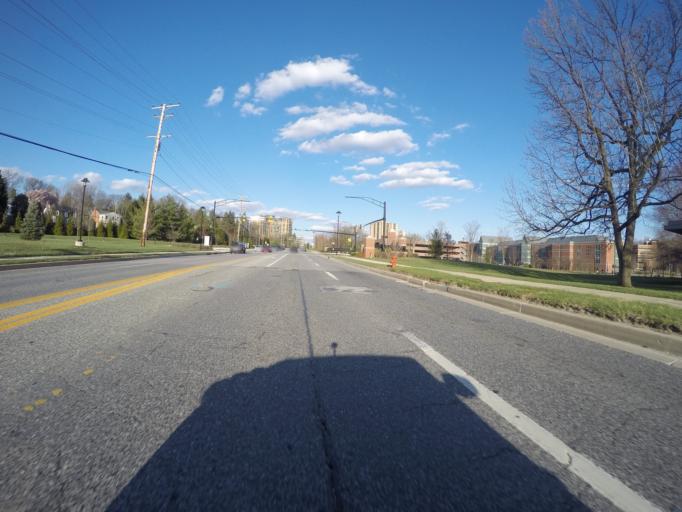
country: US
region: Maryland
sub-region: Baltimore County
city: Towson
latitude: 39.3957
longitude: -76.6140
